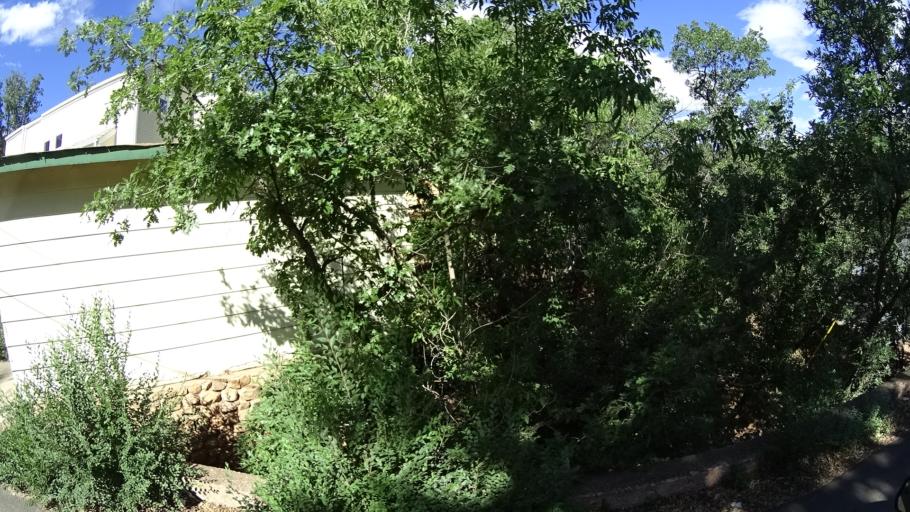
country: US
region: Colorado
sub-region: El Paso County
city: Manitou Springs
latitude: 38.8576
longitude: -104.9202
